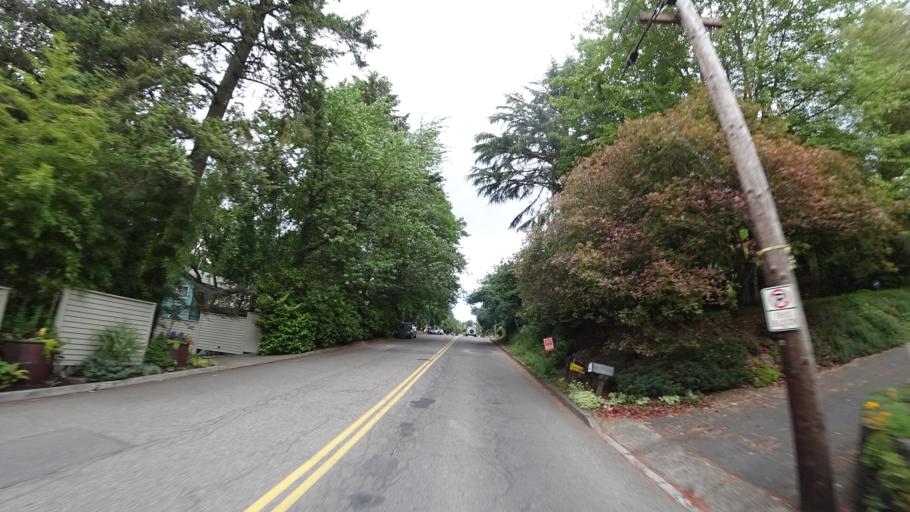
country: US
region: Oregon
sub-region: Clackamas County
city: Lake Oswego
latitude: 45.4588
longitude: -122.7037
